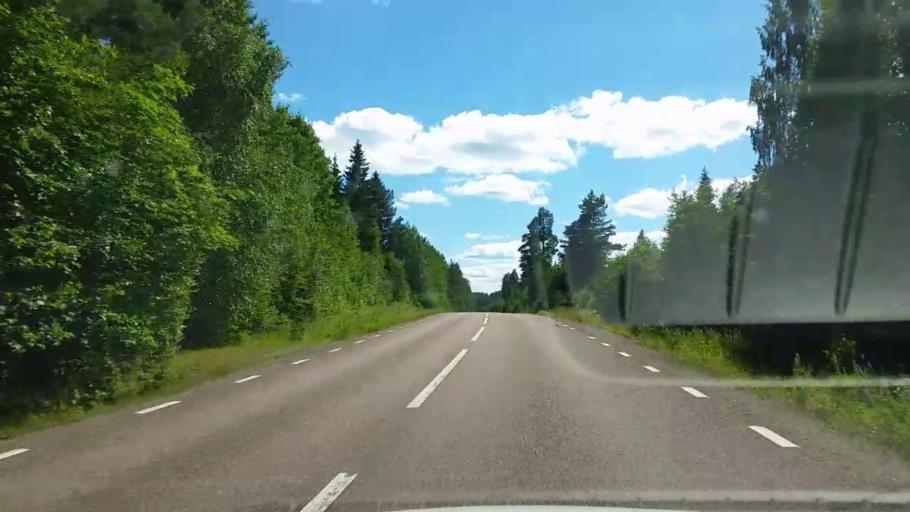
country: SE
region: Dalarna
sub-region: Faluns Kommun
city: Svardsjo
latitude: 60.9696
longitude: 15.6923
